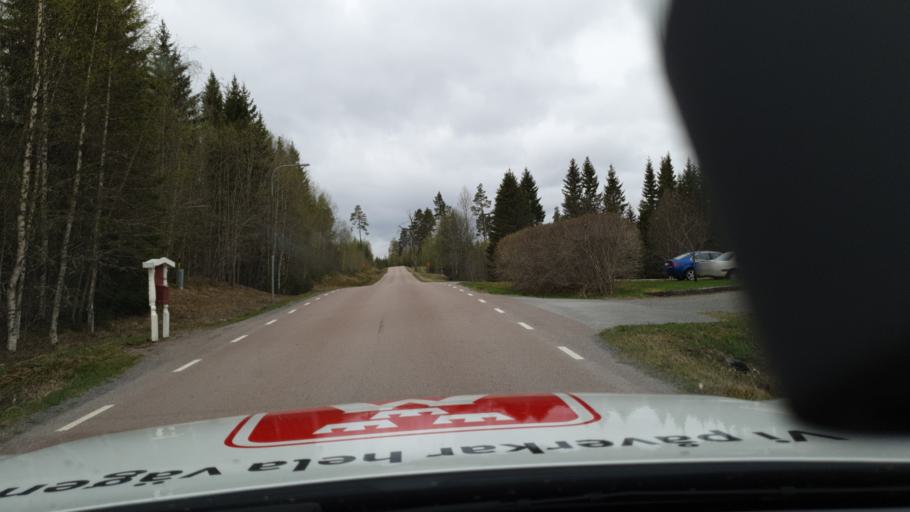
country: SE
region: Jaemtland
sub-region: OEstersunds Kommun
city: Lit
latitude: 63.3033
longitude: 14.9419
